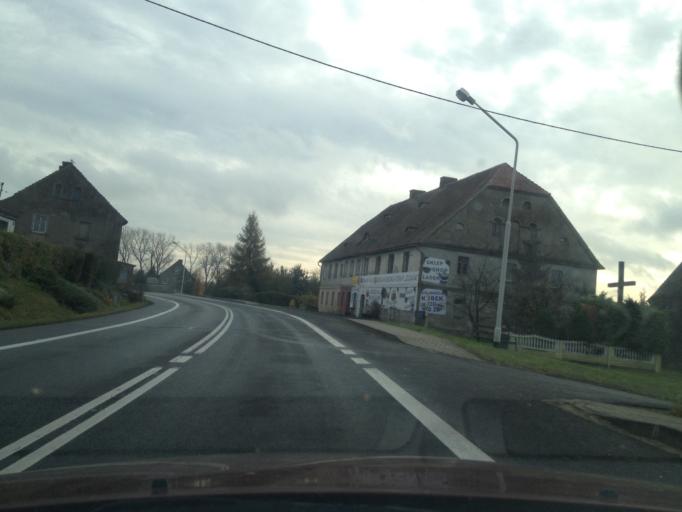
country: PL
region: Lower Silesian Voivodeship
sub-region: Powiat lubanski
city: Siekierczyn
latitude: 51.1483
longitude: 15.1740
